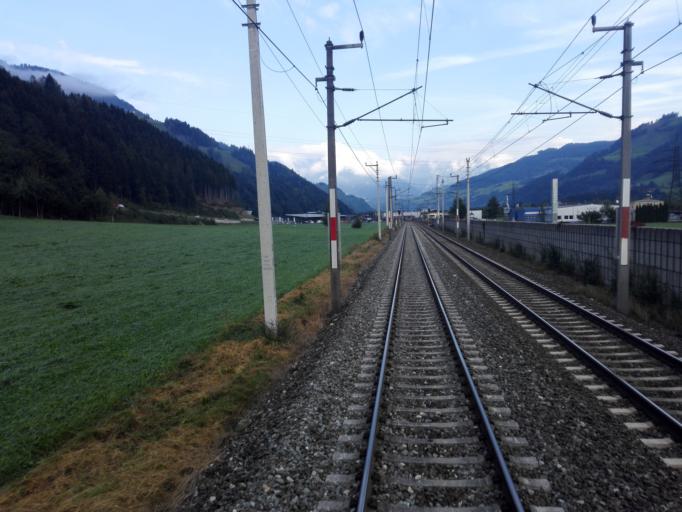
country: AT
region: Salzburg
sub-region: Politischer Bezirk Sankt Johann im Pongau
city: Sankt Johann im Pongau
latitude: 47.3637
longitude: 13.2049
